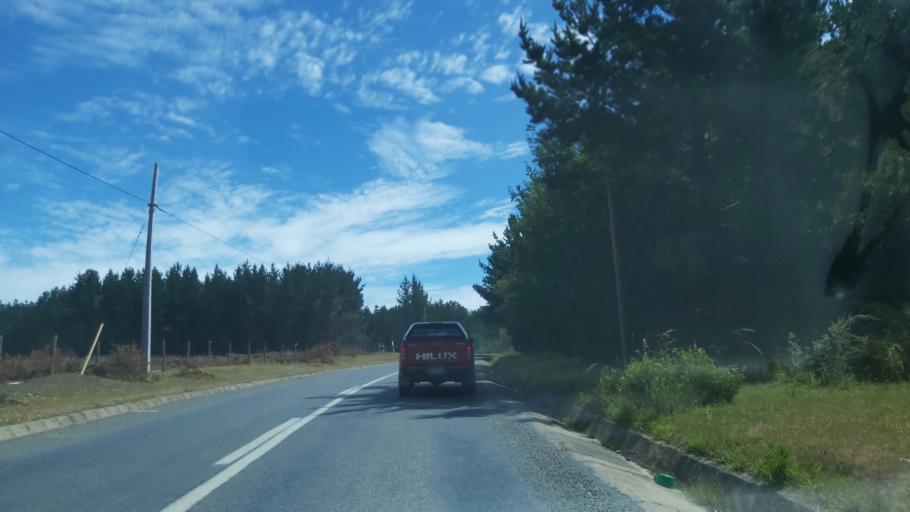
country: CL
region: Maule
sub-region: Provincia de Talca
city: Constitucion
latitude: -35.5497
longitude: -72.5670
